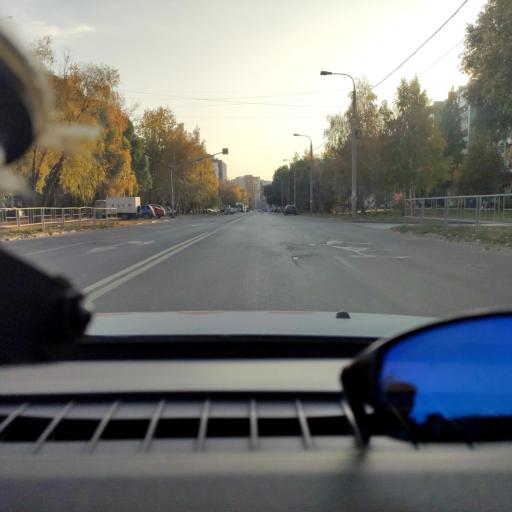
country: RU
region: Samara
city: Samara
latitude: 53.2655
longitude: 50.2303
